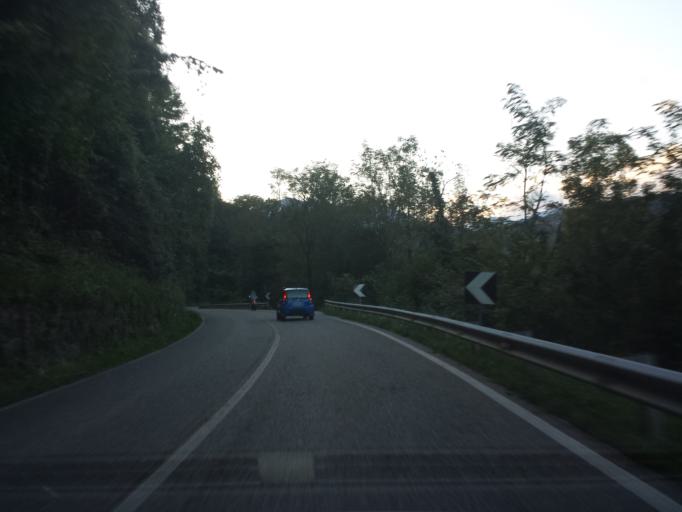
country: IT
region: Veneto
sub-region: Provincia di Vicenza
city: San Quirico
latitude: 45.6924
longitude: 11.2587
